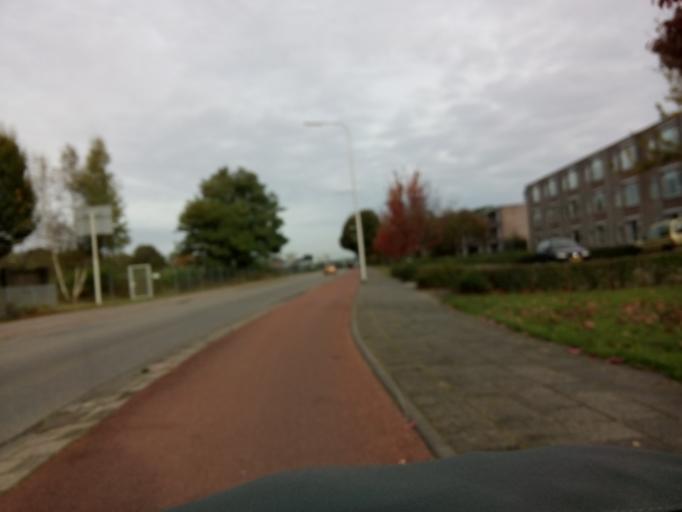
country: NL
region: Drenthe
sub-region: Gemeente Hoogeveen
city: Hoogeveen
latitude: 52.7261
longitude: 6.4682
